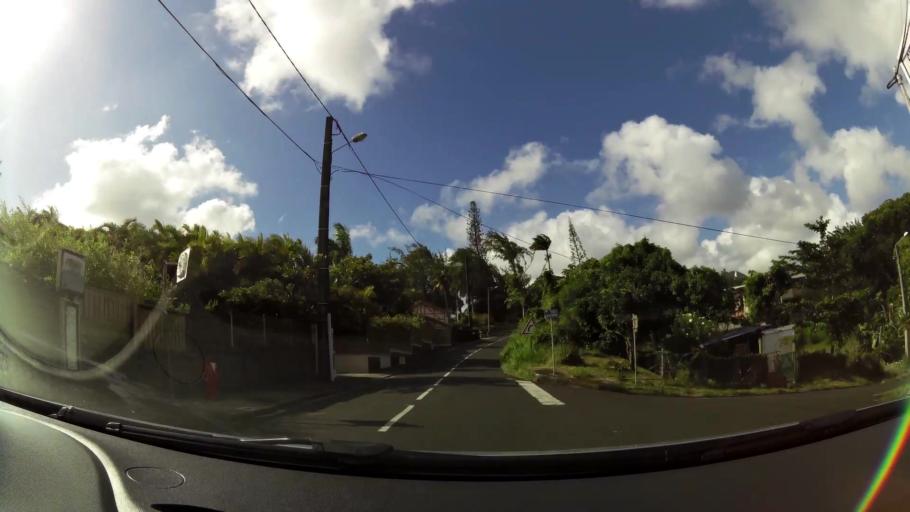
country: MQ
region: Martinique
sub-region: Martinique
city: Fort-de-France
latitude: 14.6433
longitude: -61.0780
